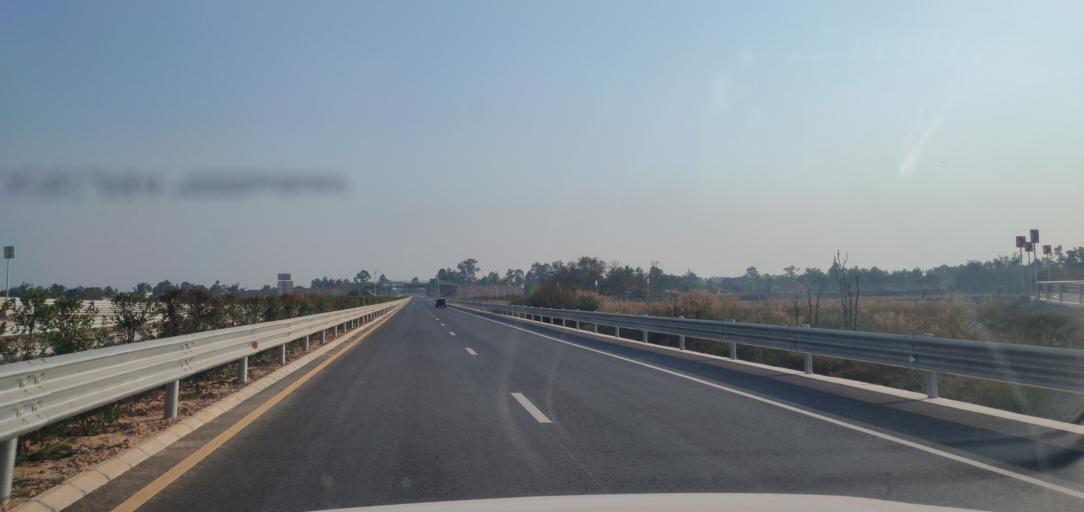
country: LA
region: Vientiane
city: Vientiane
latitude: 18.1146
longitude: 102.5023
